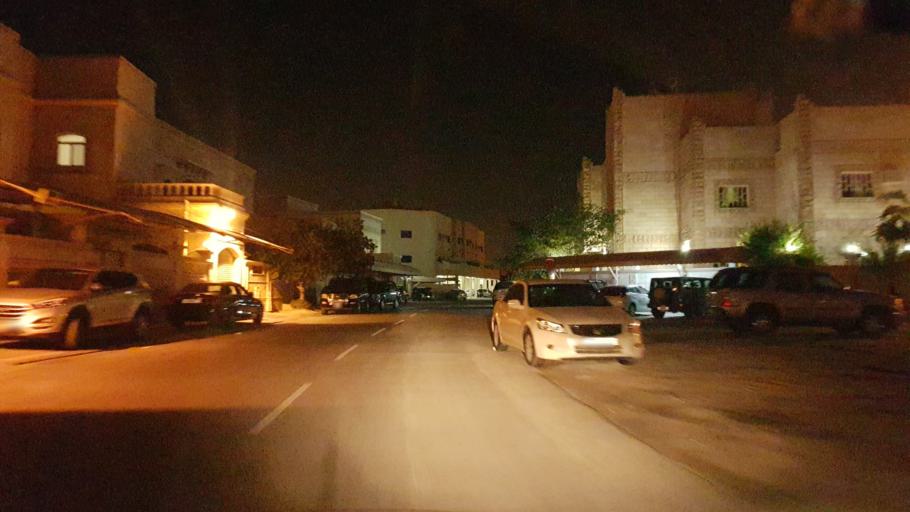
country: BH
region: Muharraq
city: Al Hadd
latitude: 26.2450
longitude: 50.6504
